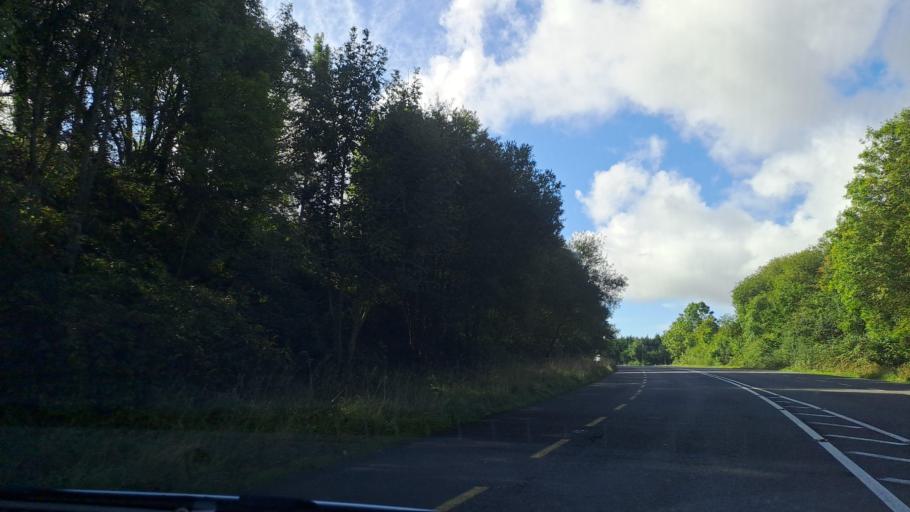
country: IE
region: Ulster
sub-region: County Monaghan
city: Carrickmacross
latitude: 53.9460
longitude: -6.7658
